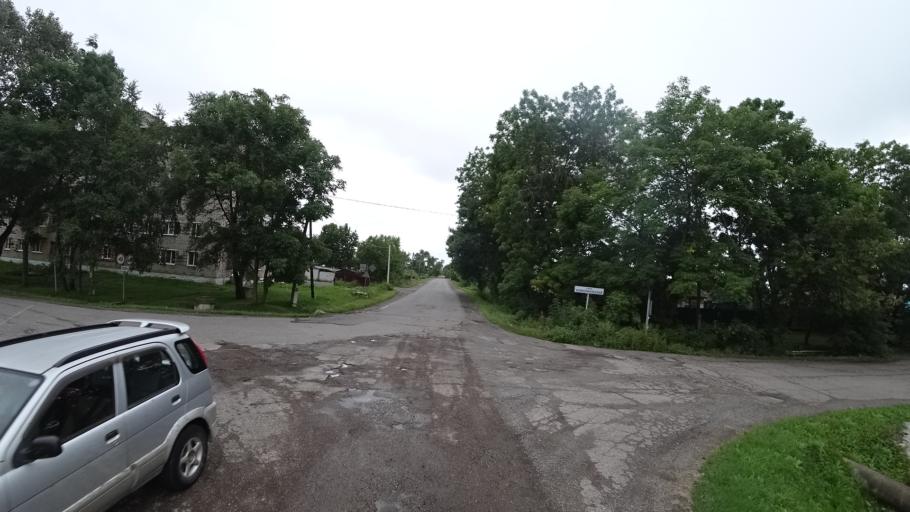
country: RU
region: Primorskiy
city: Chernigovka
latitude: 44.3464
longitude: 132.5699
